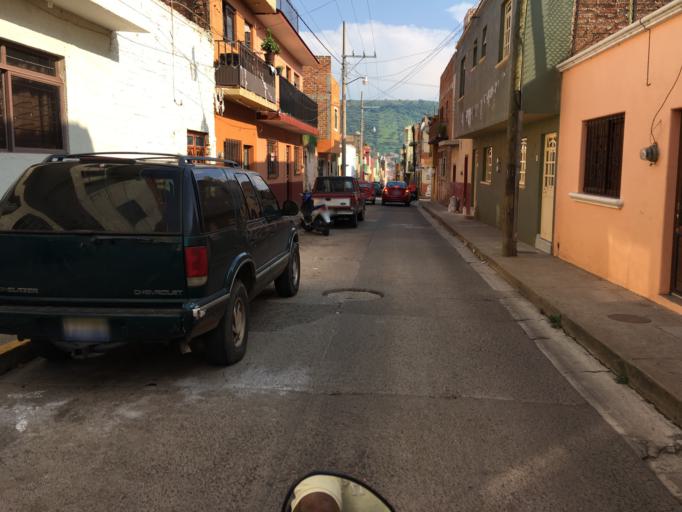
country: MX
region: Jalisco
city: Atotonilco el Alto
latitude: 20.5538
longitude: -102.5071
